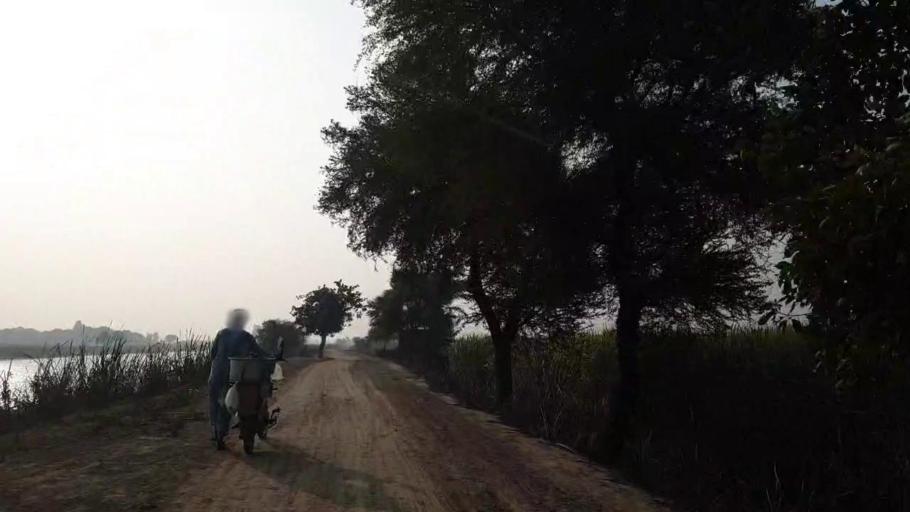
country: PK
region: Sindh
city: Tando Muhammad Khan
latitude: 25.1051
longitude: 68.5720
